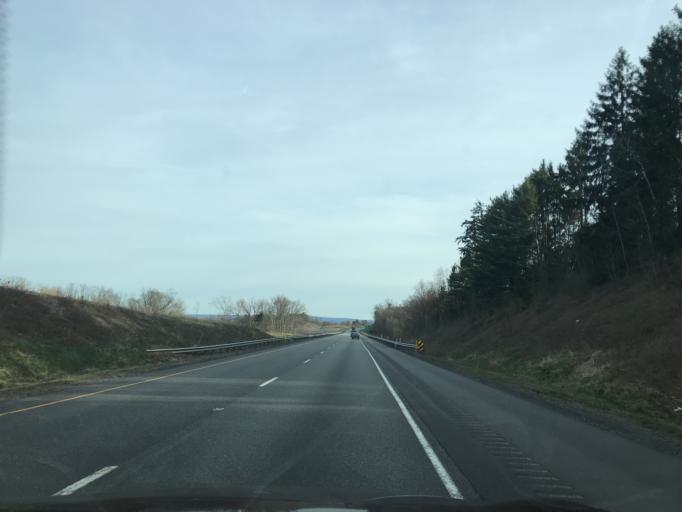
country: US
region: Pennsylvania
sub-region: Lycoming County
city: Muncy
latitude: 41.1424
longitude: -76.8021
